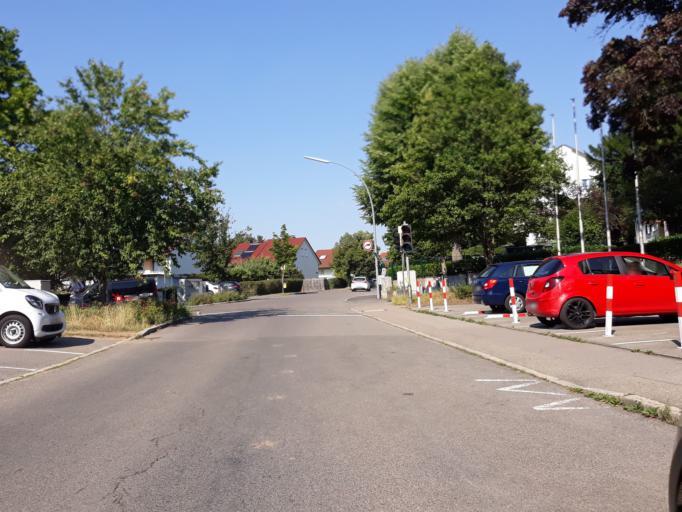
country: DE
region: Baden-Wuerttemberg
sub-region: Regierungsbezirk Stuttgart
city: Sindelfingen
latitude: 48.7023
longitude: 9.0137
